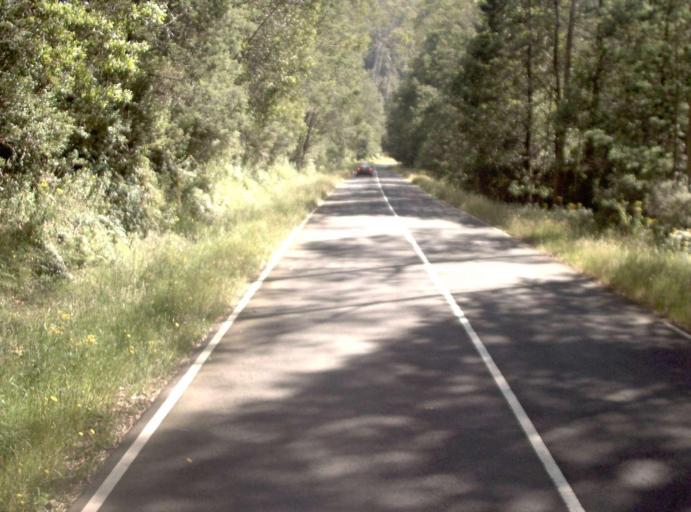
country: AU
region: Victoria
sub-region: Yarra Ranges
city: Millgrove
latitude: -37.7149
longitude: 145.6790
